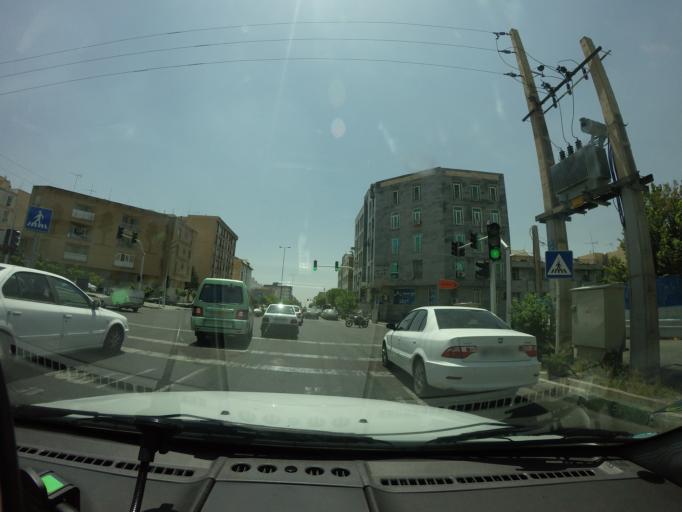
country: IR
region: Tehran
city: Tajrish
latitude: 35.7646
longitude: 51.2834
